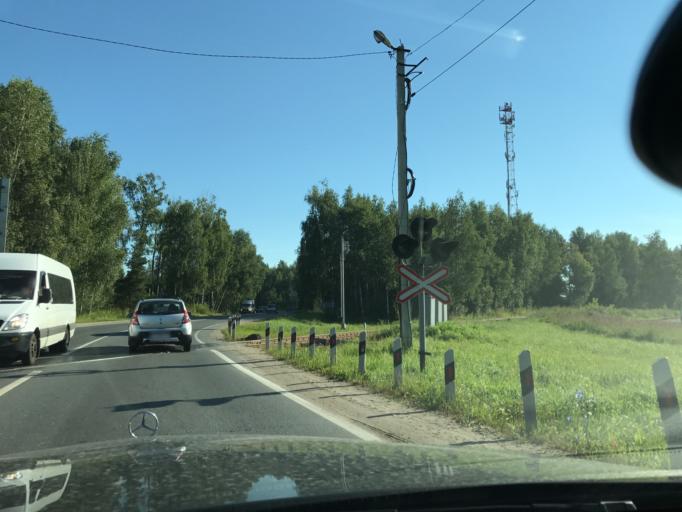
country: RU
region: Moskovskaya
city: Chernogolovka
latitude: 55.9897
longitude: 38.3503
